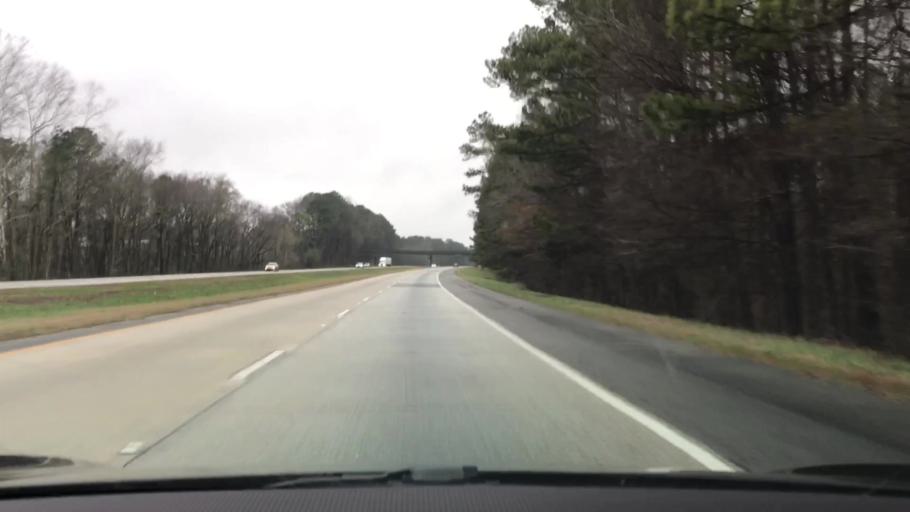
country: US
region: Georgia
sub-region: Taliaferro County
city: Crawfordville
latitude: 33.5279
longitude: -82.9527
